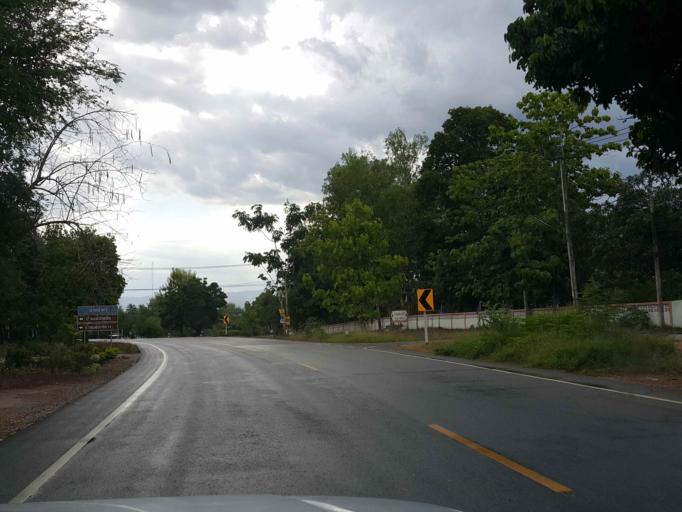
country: TH
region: Lampang
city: Thoen
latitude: 17.6526
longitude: 99.2533
